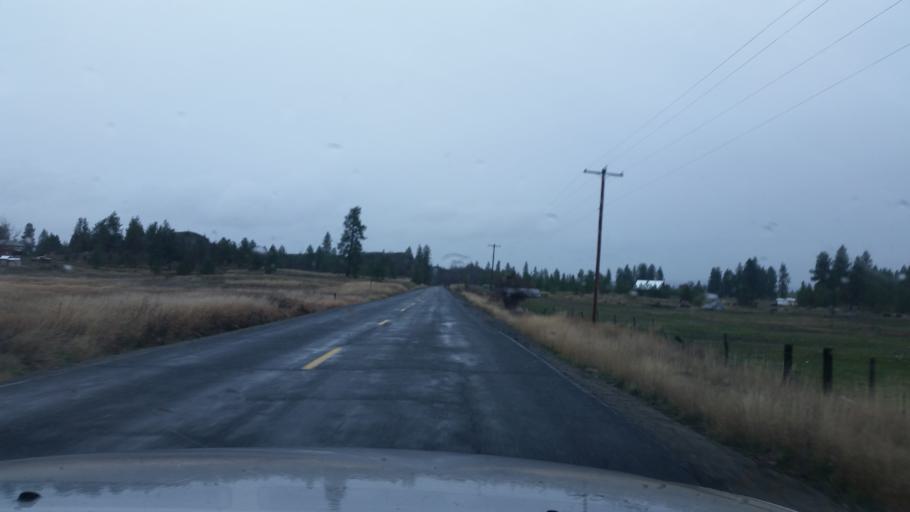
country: US
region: Washington
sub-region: Spokane County
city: Airway Heights
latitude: 47.6919
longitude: -117.5718
